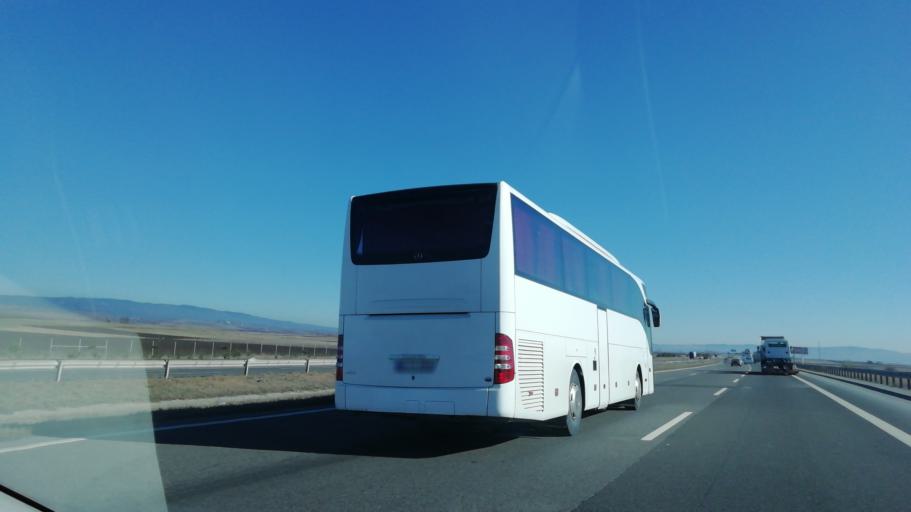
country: TR
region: Bolu
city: Dortdivan
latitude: 40.7470
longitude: 32.0932
